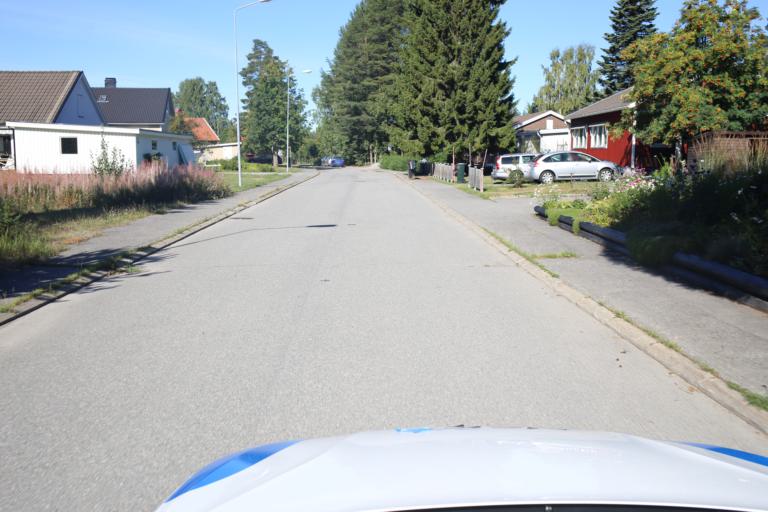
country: SE
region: Vaesterbotten
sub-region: Skelleftea Kommun
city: Viken
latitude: 64.7462
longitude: 20.7703
